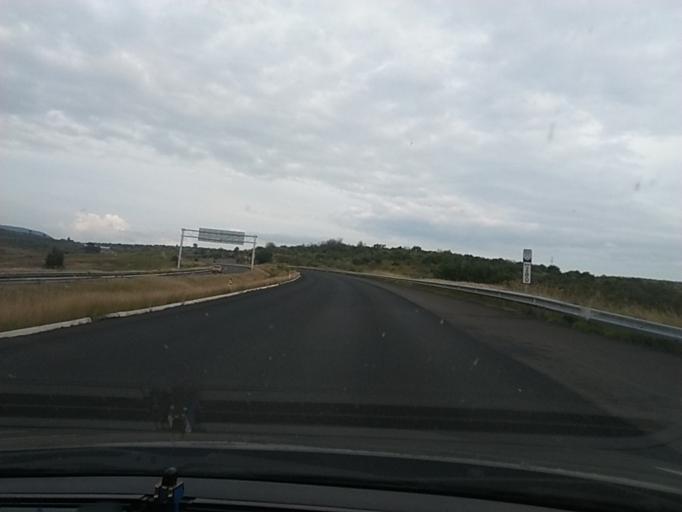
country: MX
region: Mexico
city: Huaniqueo de Morales
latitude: 19.8815
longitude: -101.5078
